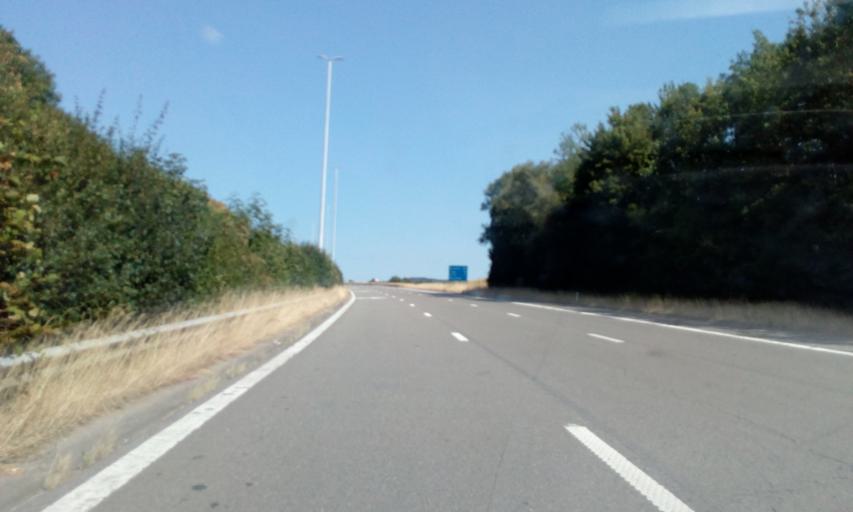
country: BE
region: Wallonia
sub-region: Province du Luxembourg
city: Aubange
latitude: 49.5695
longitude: 5.8216
